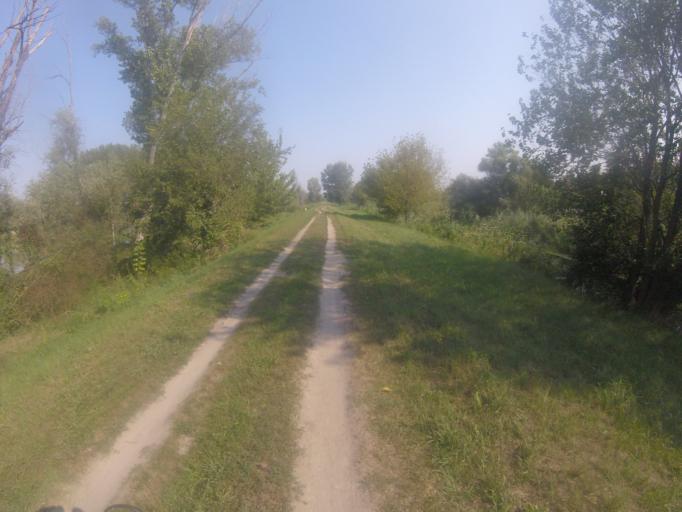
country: HU
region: Bacs-Kiskun
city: Baja
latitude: 46.2002
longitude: 18.9531
